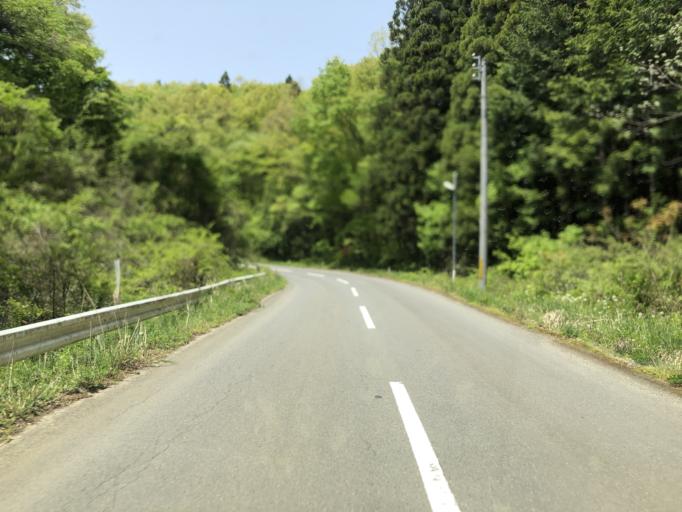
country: JP
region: Fukushima
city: Ishikawa
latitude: 37.0095
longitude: 140.3781
